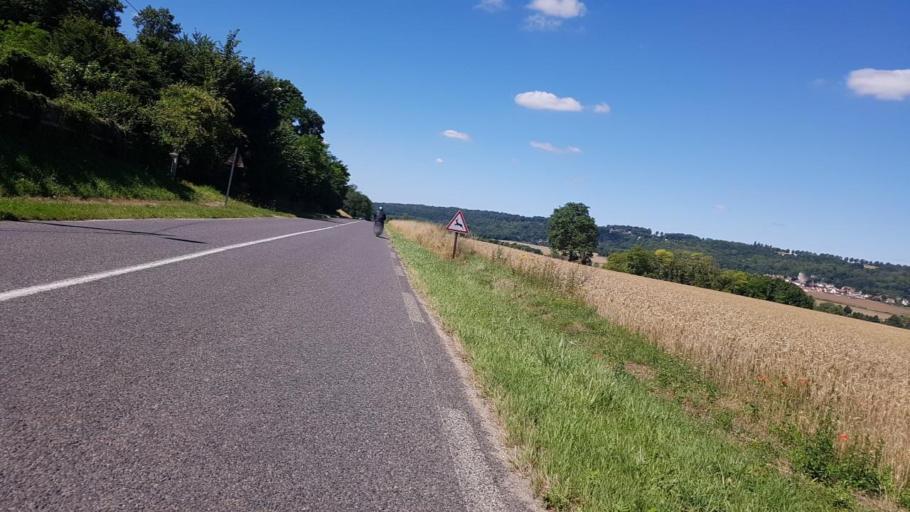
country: FR
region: Ile-de-France
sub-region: Departement de Seine-et-Marne
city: Chamigny
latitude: 48.9727
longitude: 3.1771
